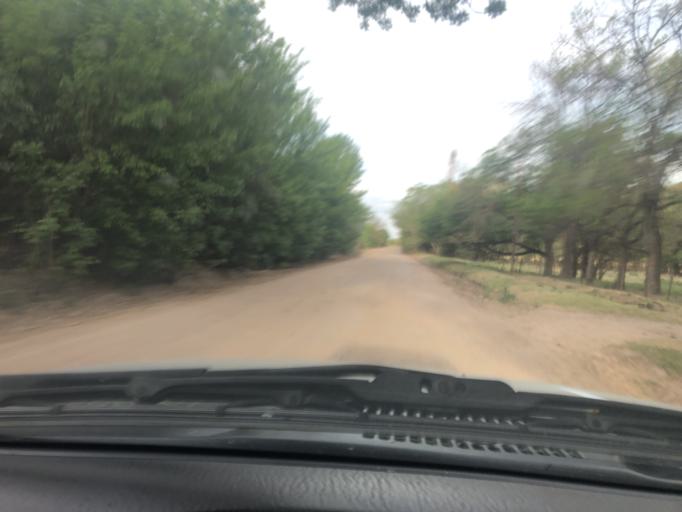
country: AR
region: Cordoba
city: La Granja
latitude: -31.0179
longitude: -64.2259
